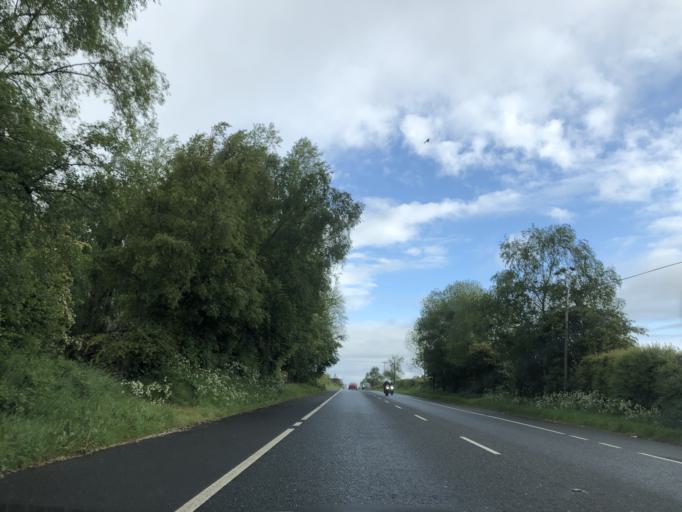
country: GB
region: Northern Ireland
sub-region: Ballymoney District
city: Ballymoney
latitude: 55.1246
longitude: -6.5530
